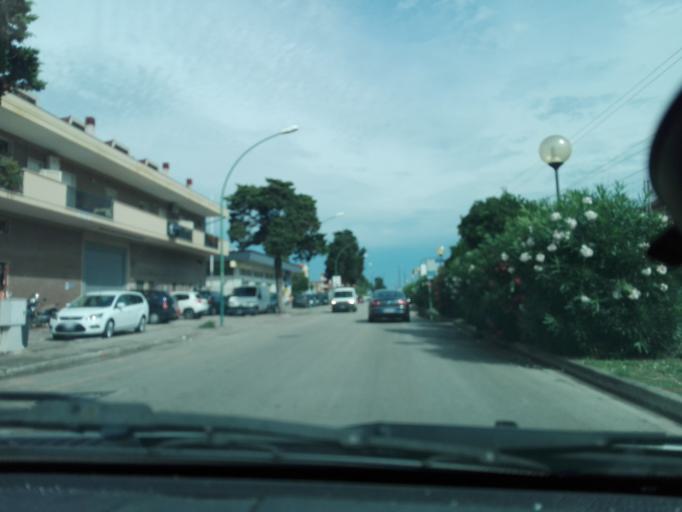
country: IT
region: Abruzzo
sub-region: Provincia di Teramo
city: Pineto
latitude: 42.6153
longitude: 14.0619
